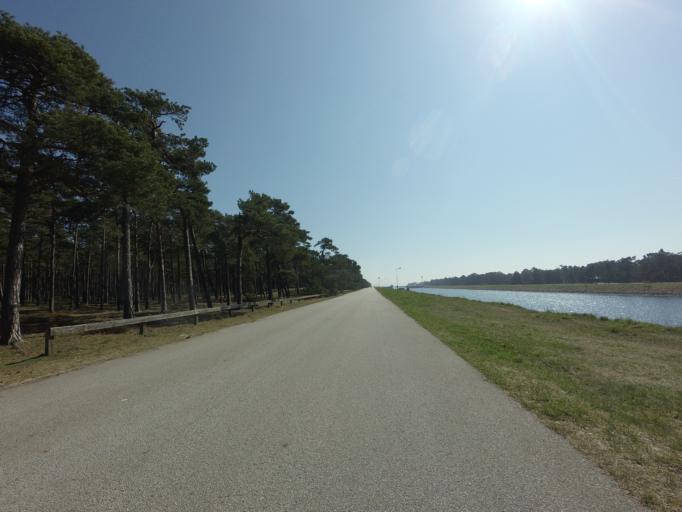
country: SE
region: Skane
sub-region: Vellinge Kommun
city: Ljunghusen
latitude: 55.4061
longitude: 12.9390
